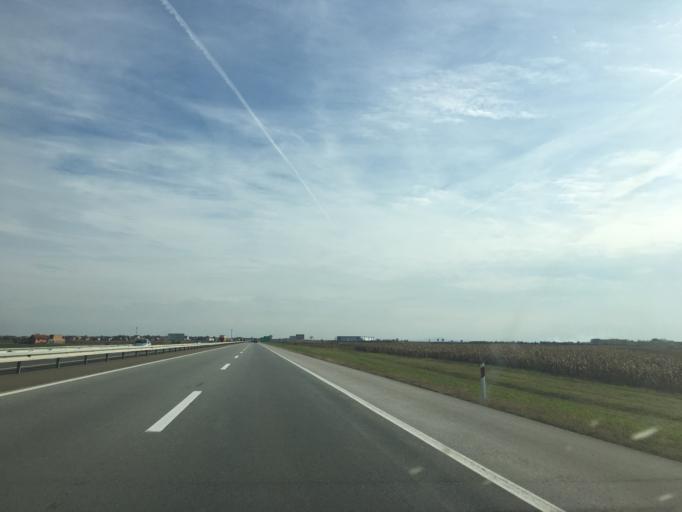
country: RS
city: Novi Banovci
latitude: 44.9554
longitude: 20.2599
